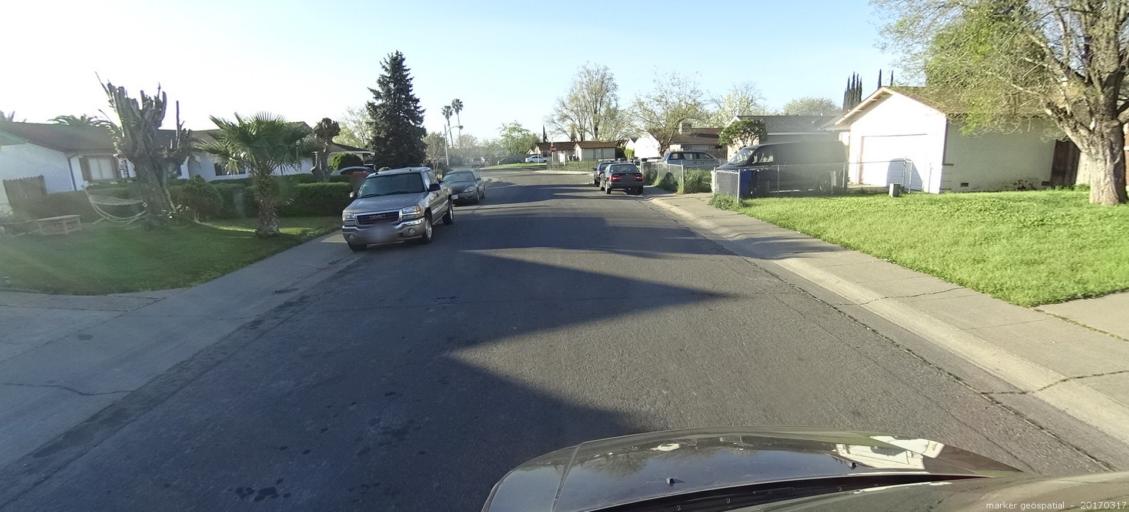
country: US
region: California
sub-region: Sacramento County
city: Parkway
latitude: 38.4872
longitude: -121.4823
